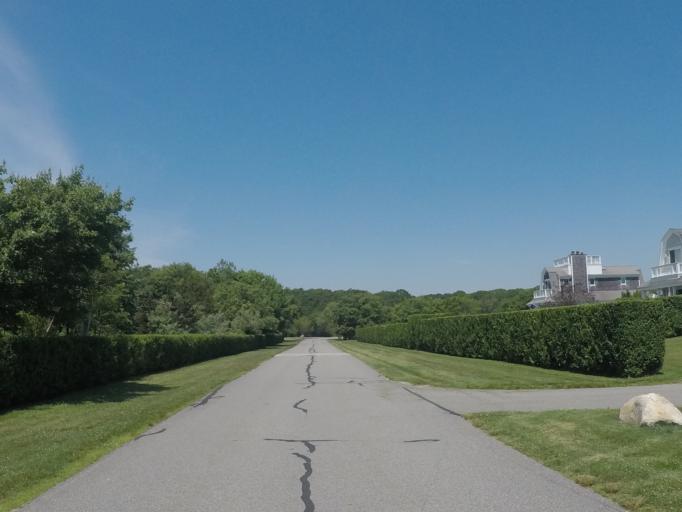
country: US
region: Massachusetts
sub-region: Bristol County
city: Bliss Corner
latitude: 41.5449
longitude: -70.9402
